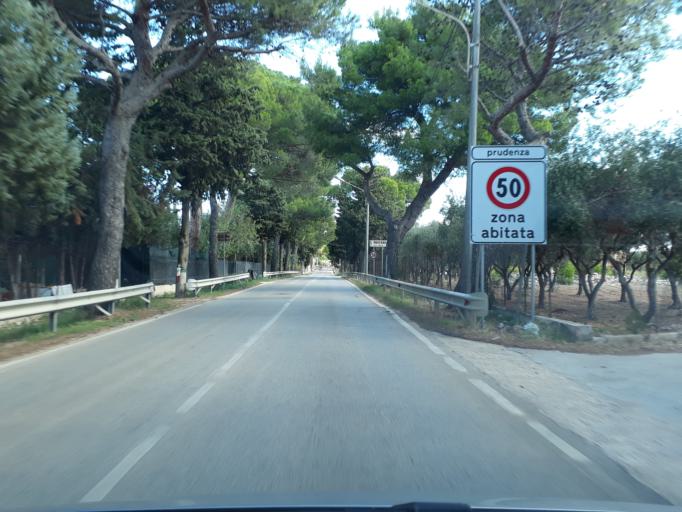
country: IT
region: Apulia
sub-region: Provincia di Bari
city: Rutigliano
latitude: 41.0318
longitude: 17.0431
